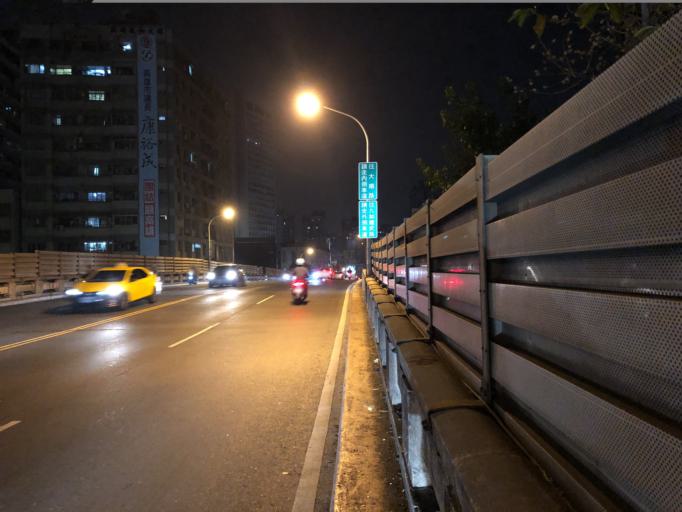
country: TW
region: Kaohsiung
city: Kaohsiung
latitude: 22.6365
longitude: 120.3272
